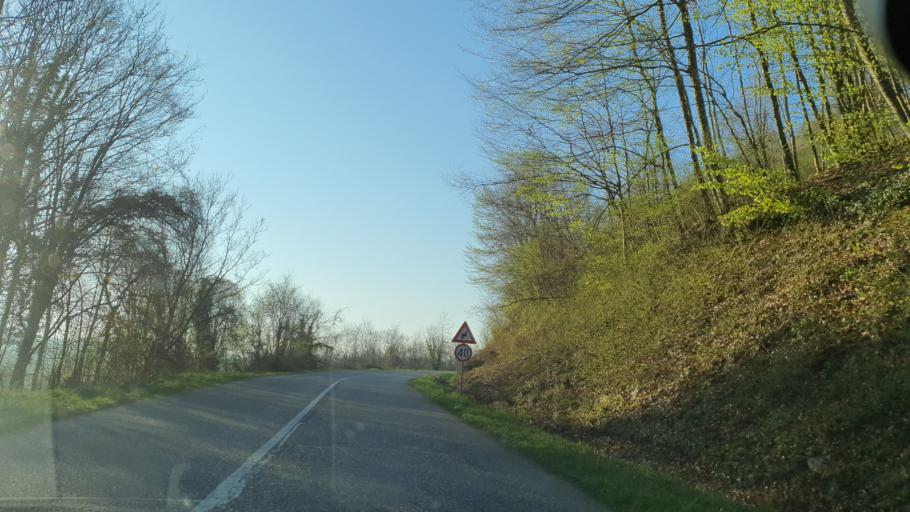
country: RS
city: Bukor
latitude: 44.4746
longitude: 19.4876
